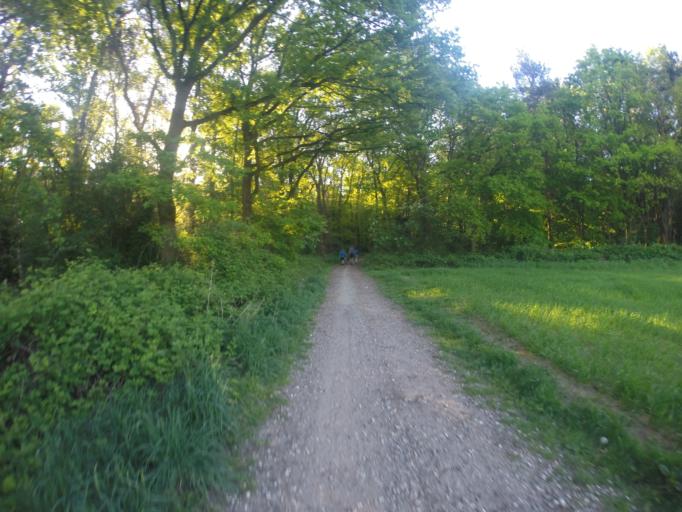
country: NL
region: Gelderland
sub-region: Gemeente Montferland
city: s-Heerenberg
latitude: 51.9085
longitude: 6.2020
